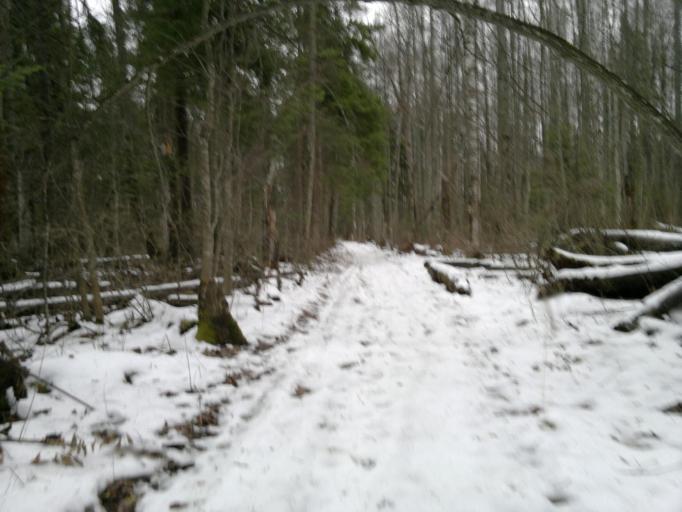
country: RU
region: Mariy-El
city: Yoshkar-Ola
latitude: 56.6092
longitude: 47.9565
